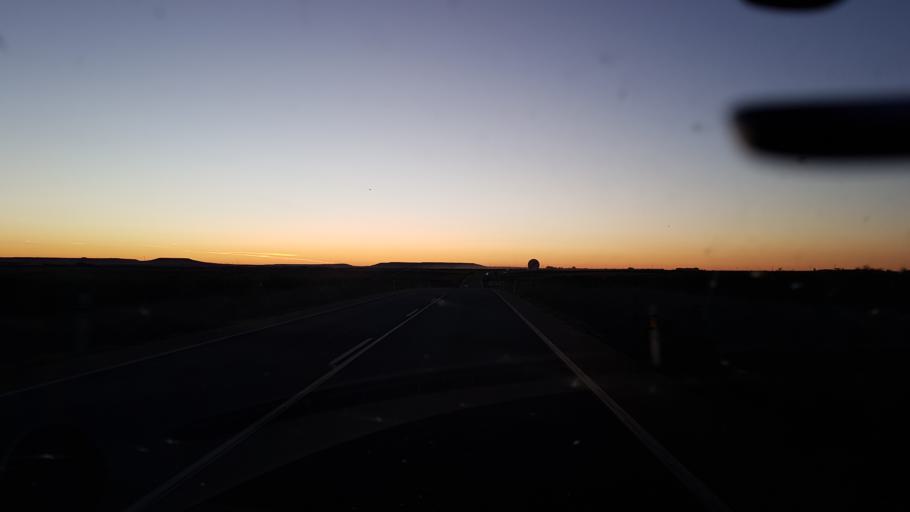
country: ES
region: Castille and Leon
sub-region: Provincia de Zamora
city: Toro
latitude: 41.5316
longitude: -5.3540
